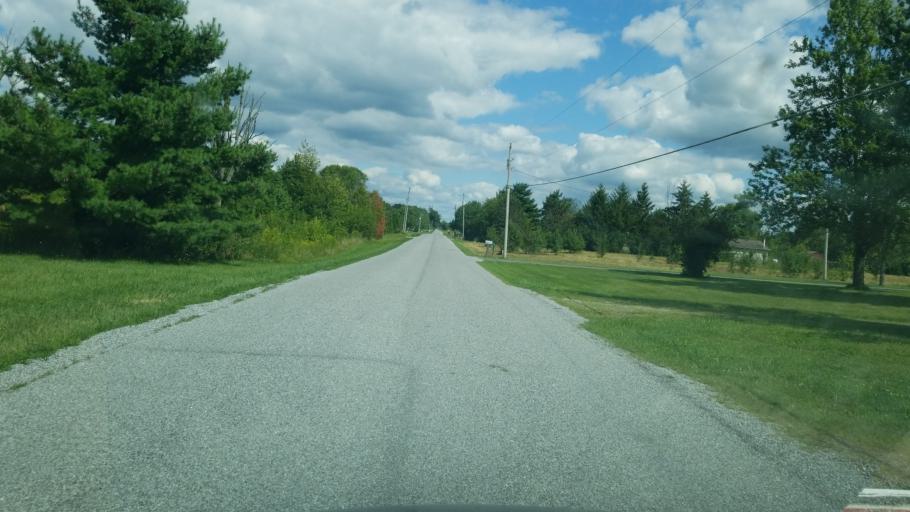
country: US
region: Ohio
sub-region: Allen County
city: Lima
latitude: 40.7169
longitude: -83.9821
